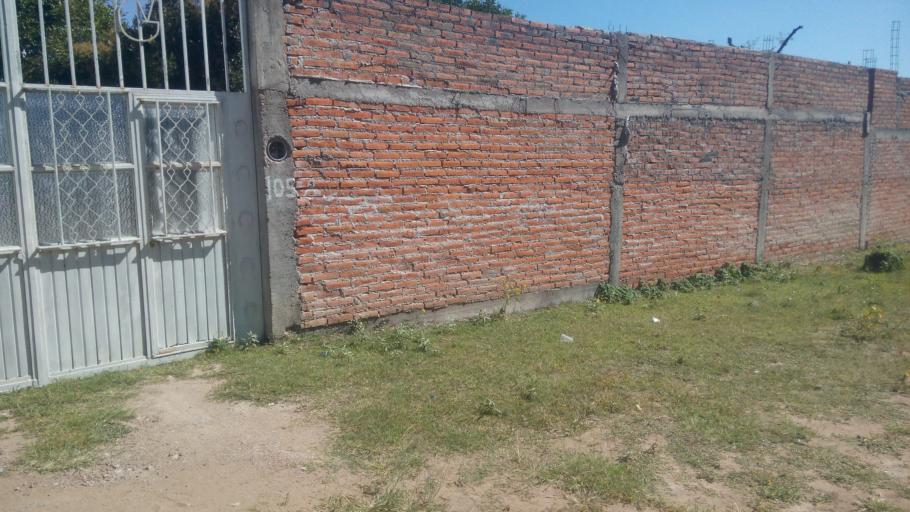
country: MX
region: Aguascalientes
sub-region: Aguascalientes
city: San Sebastian [Fraccionamiento]
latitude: 21.7812
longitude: -102.2369
